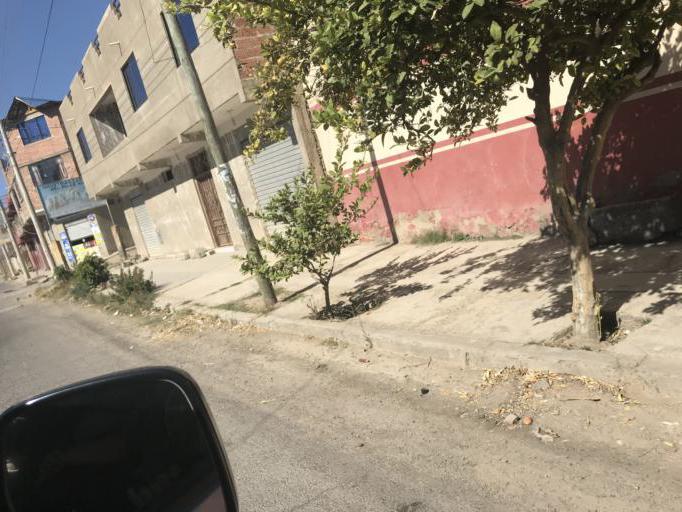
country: BO
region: Cochabamba
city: Punata
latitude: -17.5499
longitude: -65.8469
